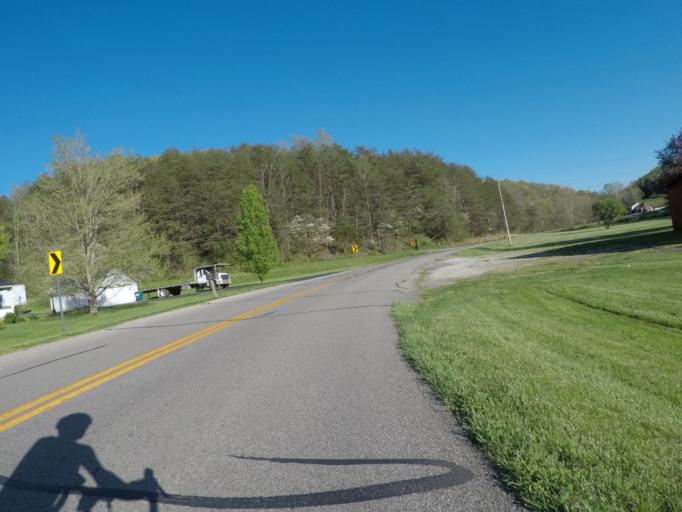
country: US
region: Kentucky
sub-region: Boyd County
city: Meads
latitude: 38.3659
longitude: -82.6789
